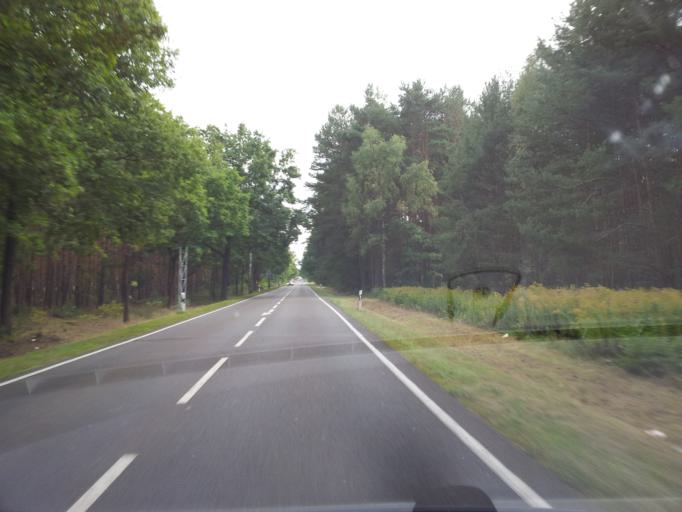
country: DE
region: Brandenburg
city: Schwarzbach
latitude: 51.4342
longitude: 13.9090
